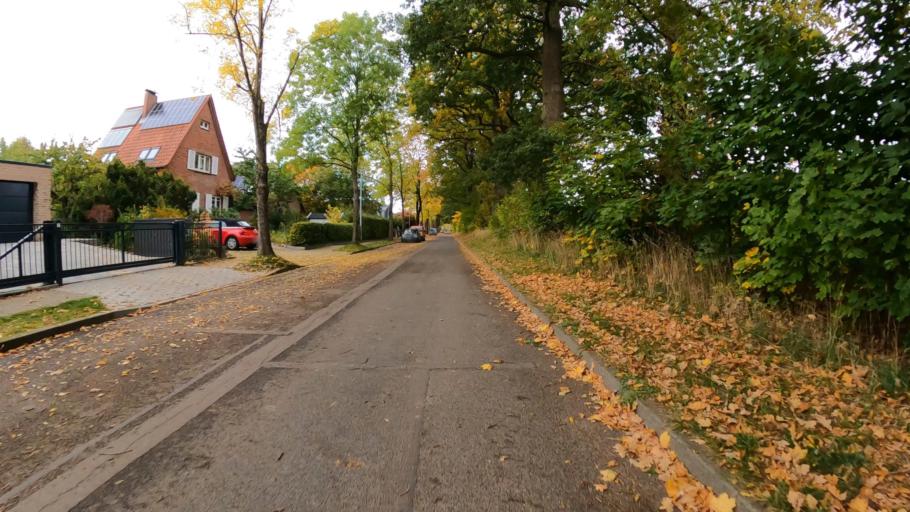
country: DE
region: Schleswig-Holstein
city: Ahrensburg
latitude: 53.6519
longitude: 10.2442
